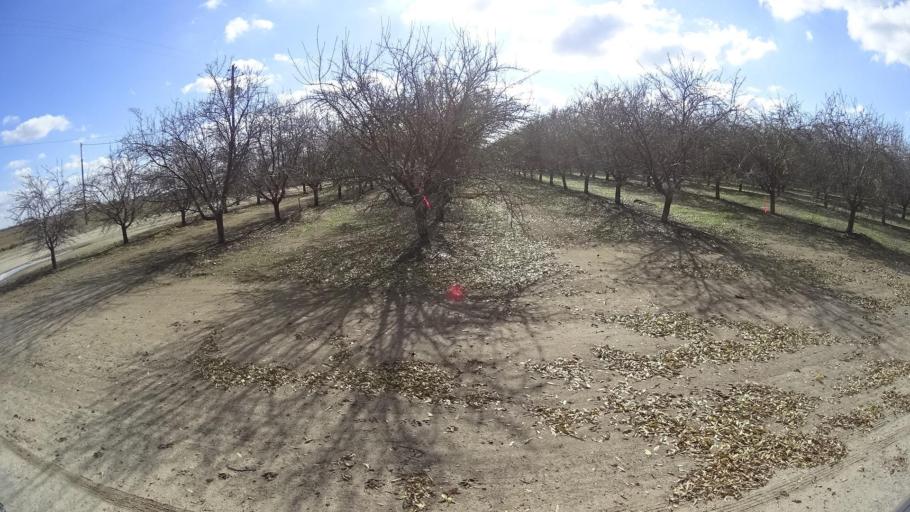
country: US
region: California
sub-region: Kern County
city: Delano
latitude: 35.7467
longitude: -119.3480
